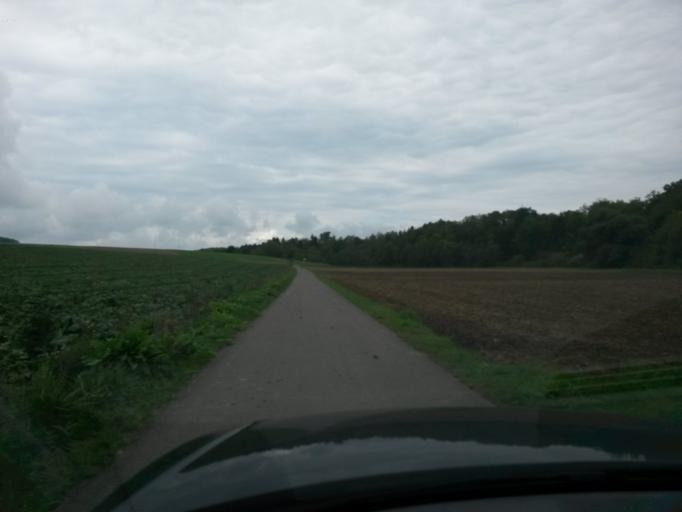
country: DE
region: Bavaria
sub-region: Regierungsbezirk Unterfranken
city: Gadheim
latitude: 49.8461
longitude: 9.9136
